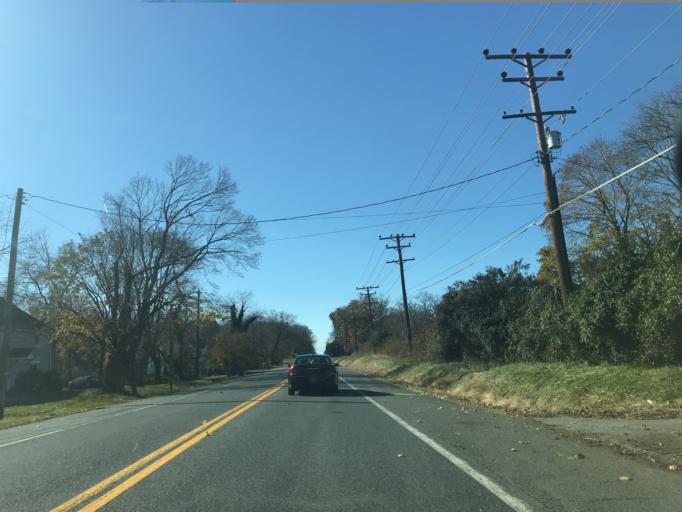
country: US
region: Maryland
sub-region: Harford County
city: South Bel Air
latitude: 39.5513
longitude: -76.2949
